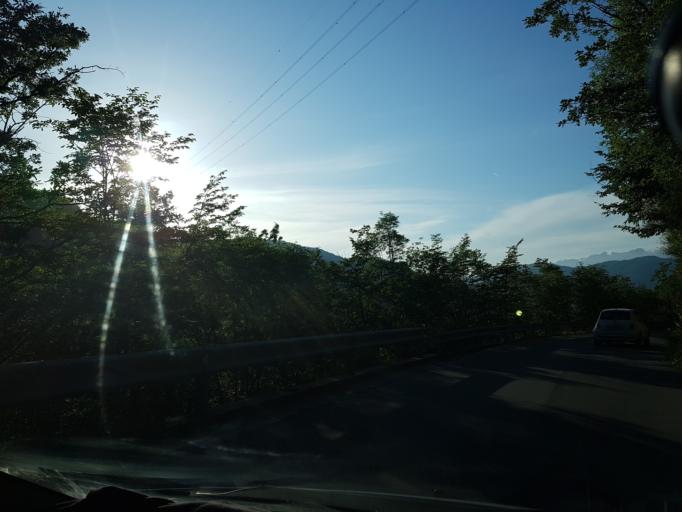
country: IT
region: Tuscany
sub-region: Provincia di Lucca
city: Minucciano
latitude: 44.1742
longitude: 10.2008
